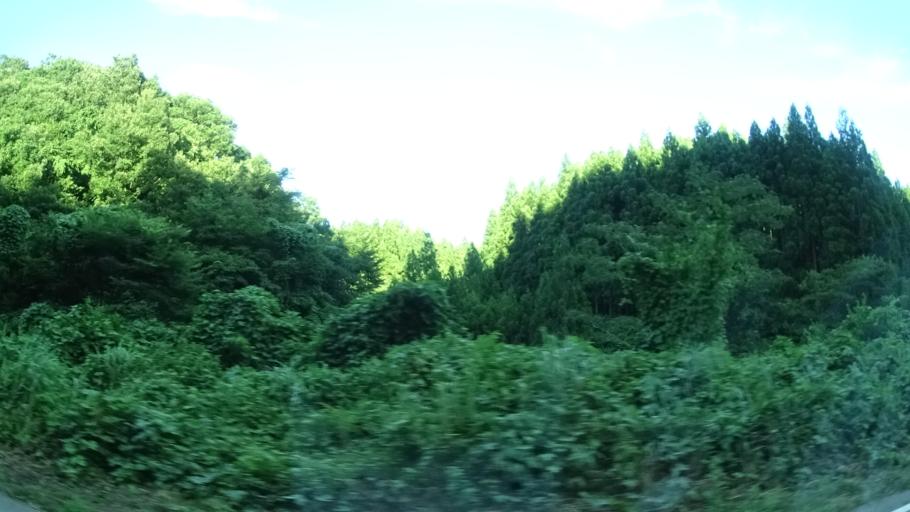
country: JP
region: Ishikawa
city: Nanao
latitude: 37.2689
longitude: 136.8848
